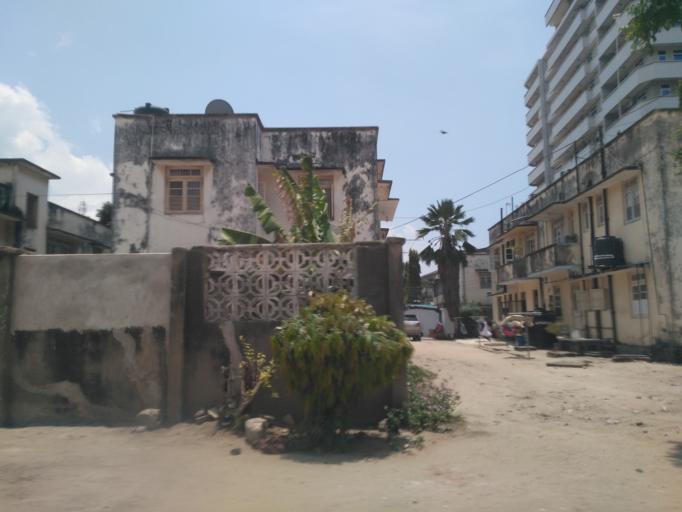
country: TZ
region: Dar es Salaam
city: Dar es Salaam
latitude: -6.8105
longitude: 39.2761
